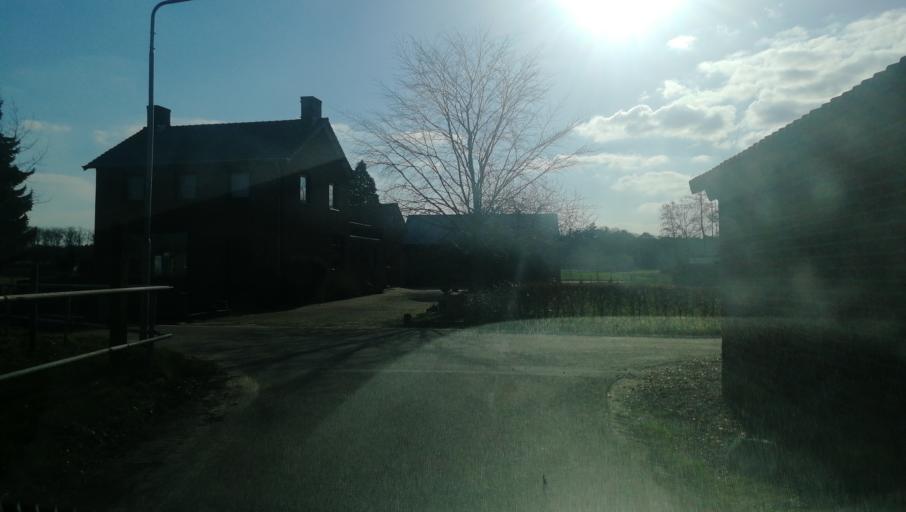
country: NL
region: Limburg
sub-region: Gemeente Venlo
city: Tegelen
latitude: 51.3729
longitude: 6.1115
